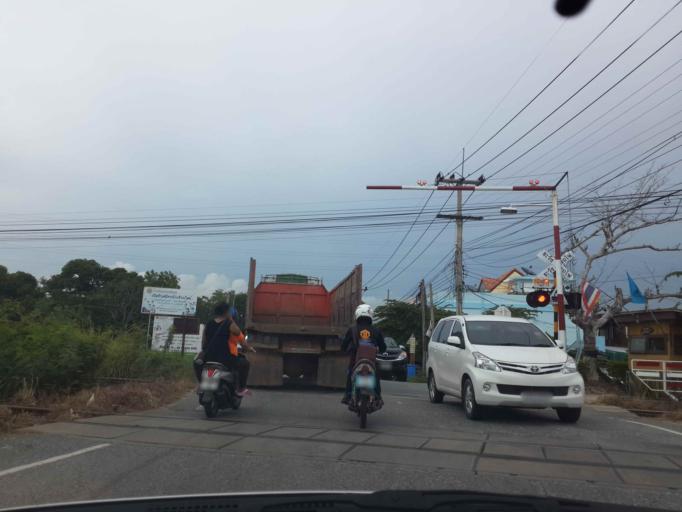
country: TH
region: Chon Buri
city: Si Racha
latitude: 13.2129
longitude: 100.9480
